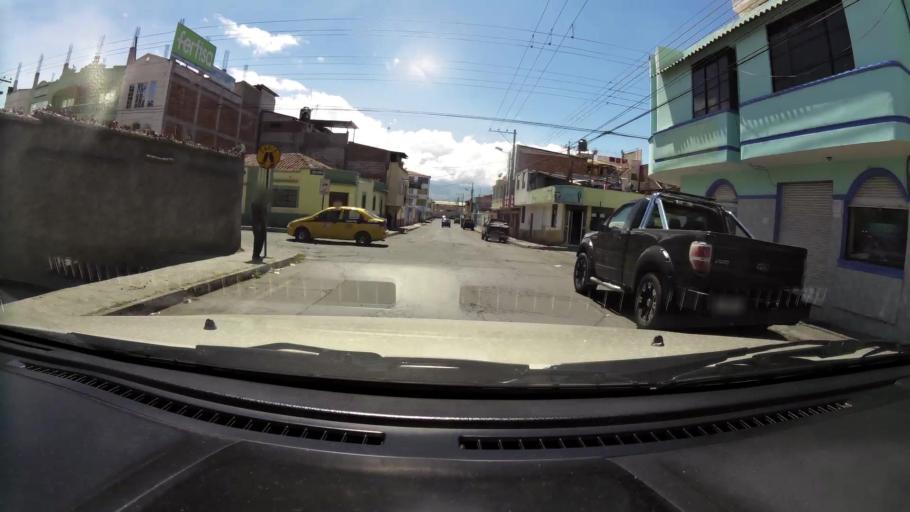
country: EC
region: Chimborazo
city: Riobamba
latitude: -1.6645
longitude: -78.6480
